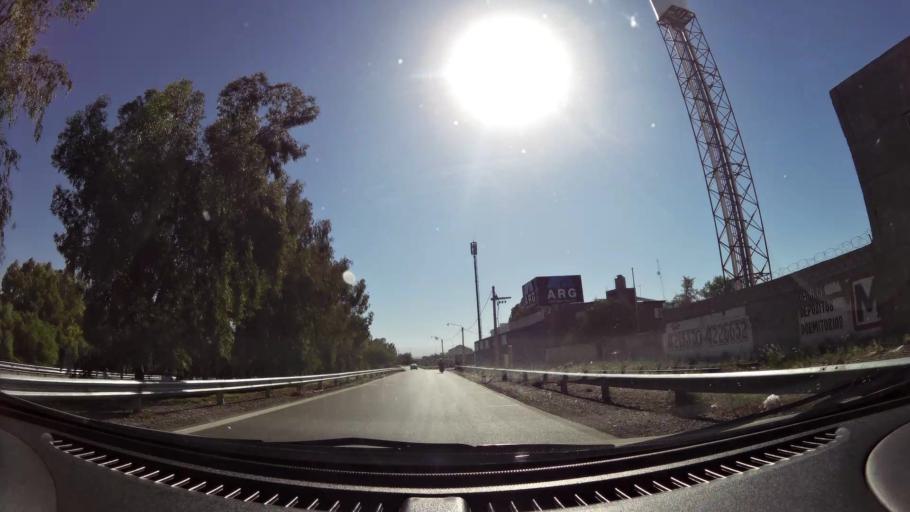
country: AR
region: San Juan
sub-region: Departamento de Santa Lucia
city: Santa Lucia
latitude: -31.5161
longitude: -68.5142
